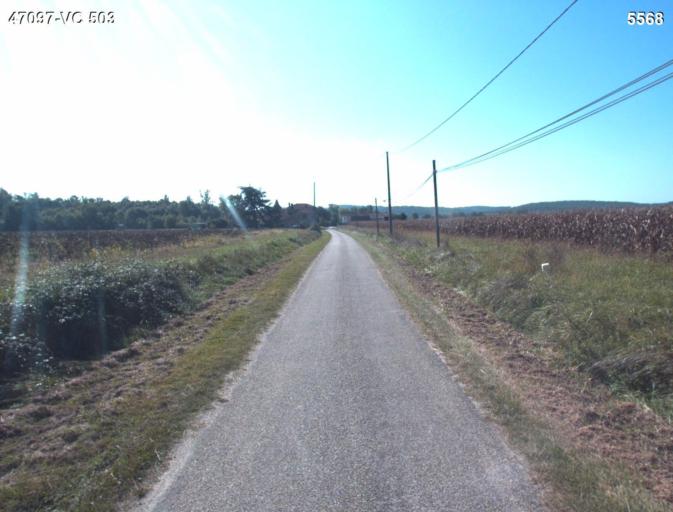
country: FR
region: Aquitaine
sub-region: Departement du Lot-et-Garonne
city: Port-Sainte-Marie
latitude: 44.2335
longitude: 0.3874
